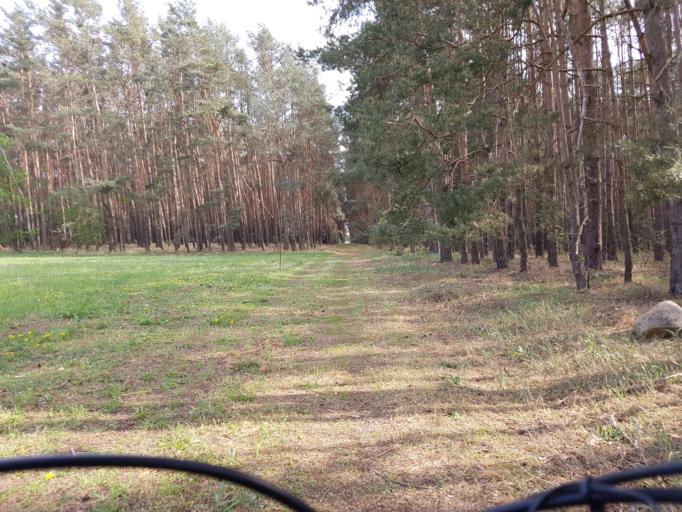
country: DE
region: Brandenburg
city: Schilda
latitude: 51.5970
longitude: 13.3762
